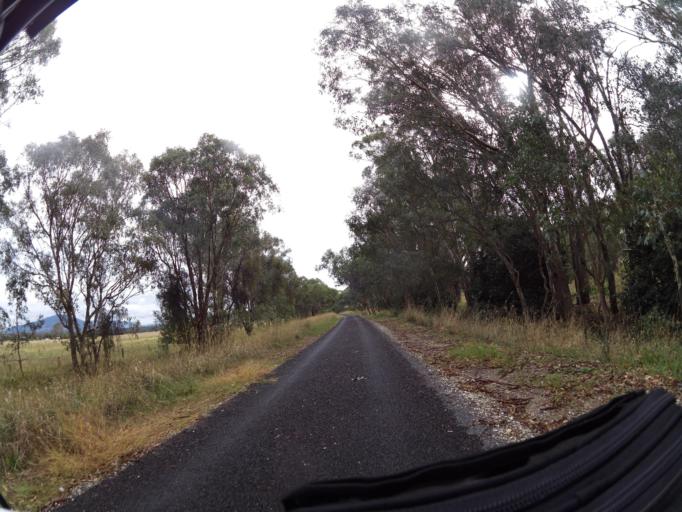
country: AU
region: New South Wales
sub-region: Albury Municipality
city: East Albury
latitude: -36.1395
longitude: 146.9873
